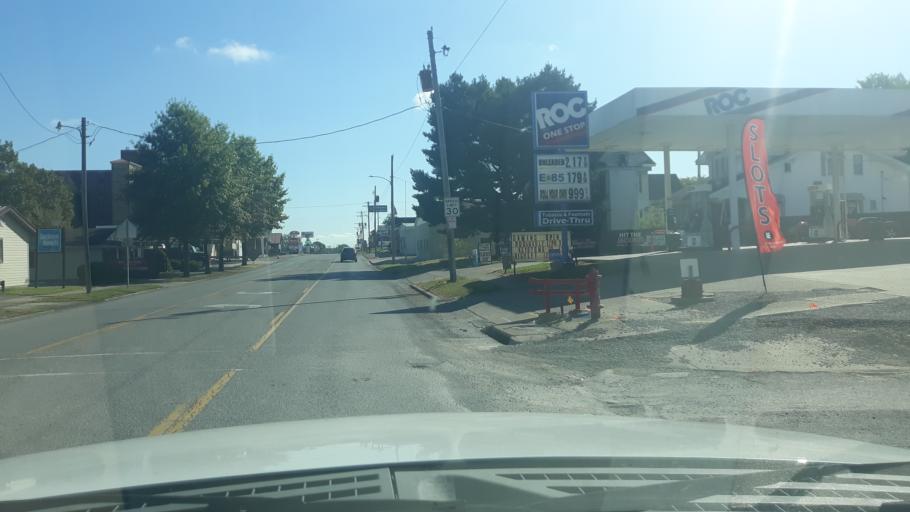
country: US
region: Illinois
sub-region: Saline County
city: Harrisburg
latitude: 37.7383
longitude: -88.5379
